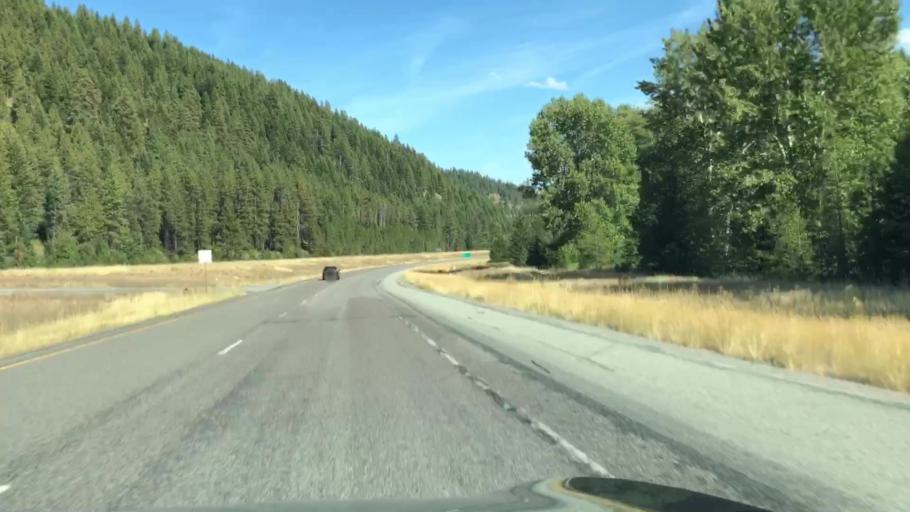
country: US
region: Montana
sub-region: Sanders County
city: Thompson Falls
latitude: 47.4074
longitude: -115.4969
